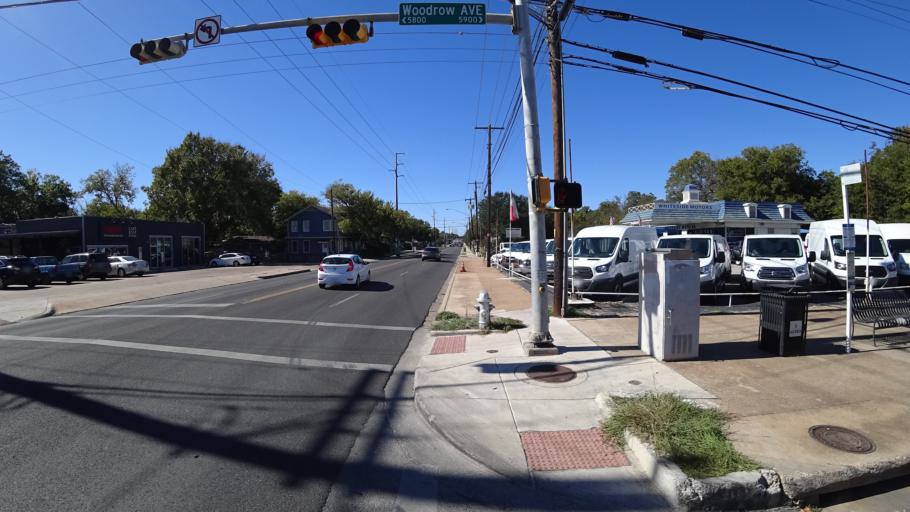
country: US
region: Texas
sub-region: Travis County
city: Austin
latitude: 30.3310
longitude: -97.7316
